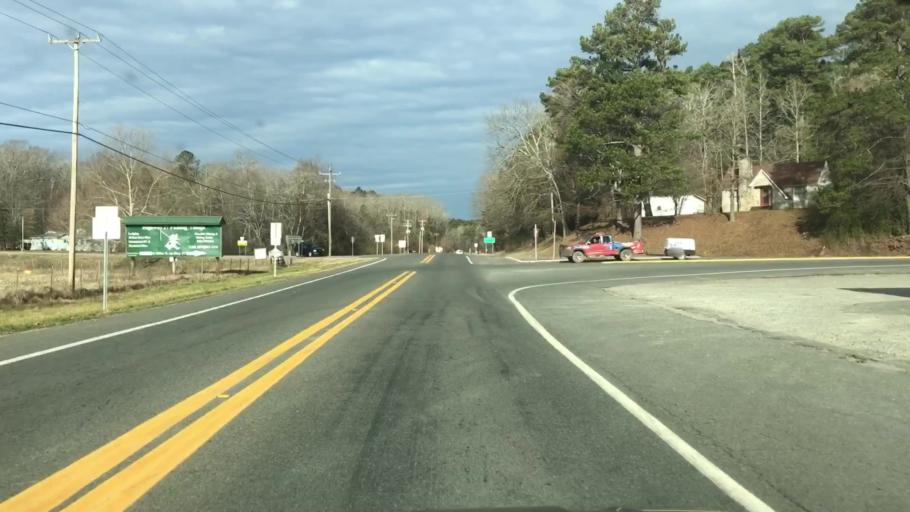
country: US
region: Arkansas
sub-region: Montgomery County
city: Mount Ida
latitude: 34.5620
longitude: -93.6394
